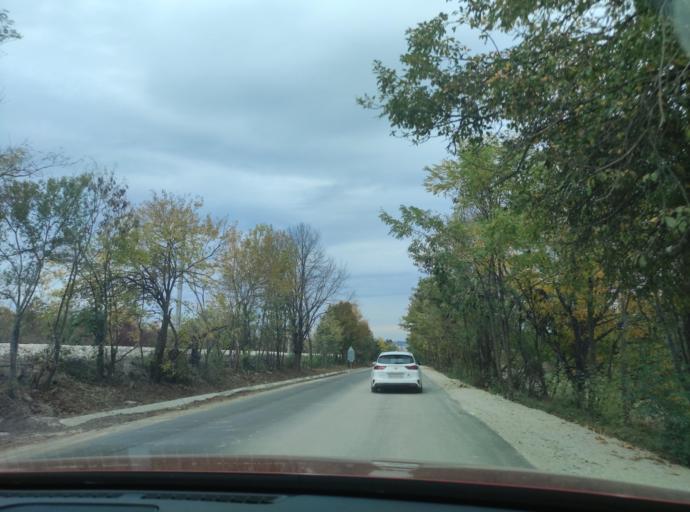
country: BG
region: Montana
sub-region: Obshtina Montana
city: Montana
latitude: 43.3873
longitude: 23.2430
